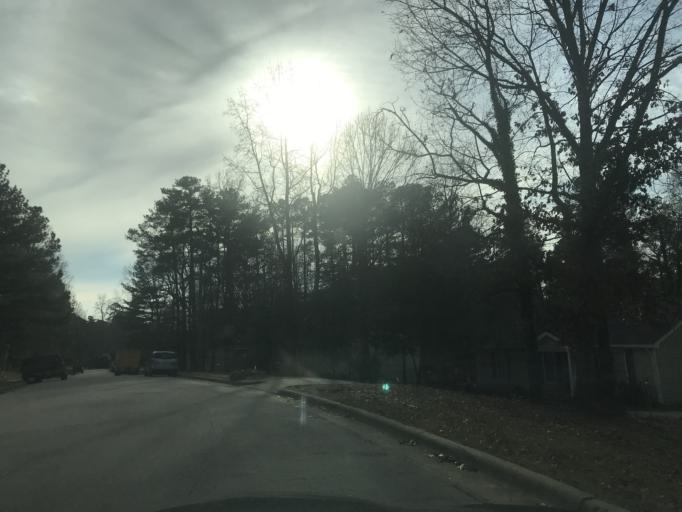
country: US
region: North Carolina
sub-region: Wake County
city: Raleigh
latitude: 35.8318
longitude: -78.5892
